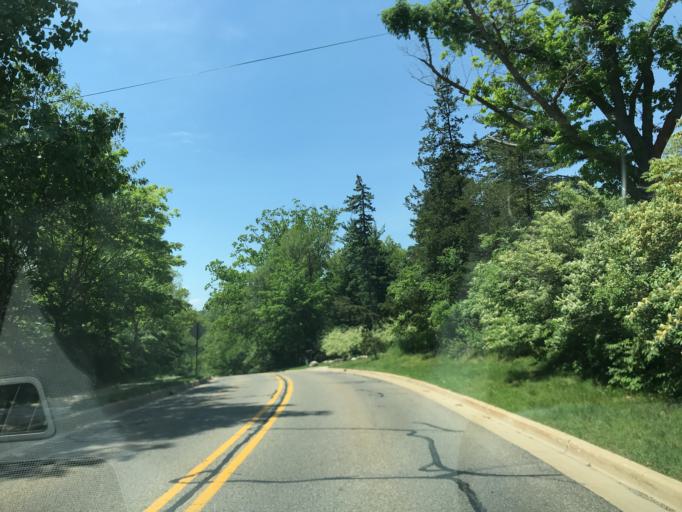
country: US
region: Michigan
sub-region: Washtenaw County
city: Ann Arbor
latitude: 42.2881
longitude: -83.6998
